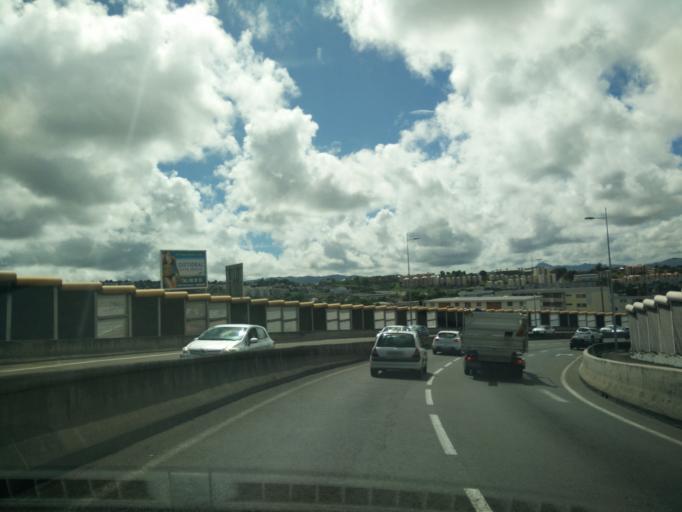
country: MQ
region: Martinique
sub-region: Martinique
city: Fort-de-France
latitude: 14.6164
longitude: -61.0548
